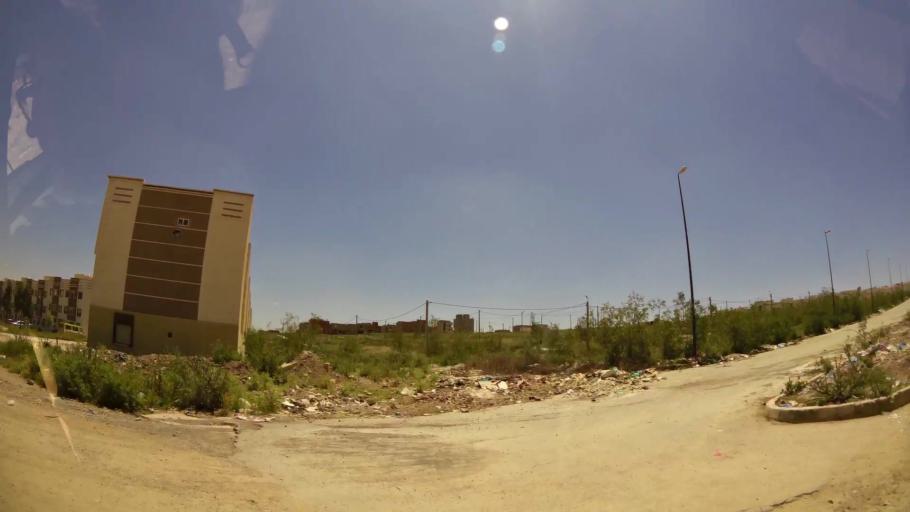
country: MA
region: Oriental
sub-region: Oujda-Angad
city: Oujda
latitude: 34.6554
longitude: -1.9465
